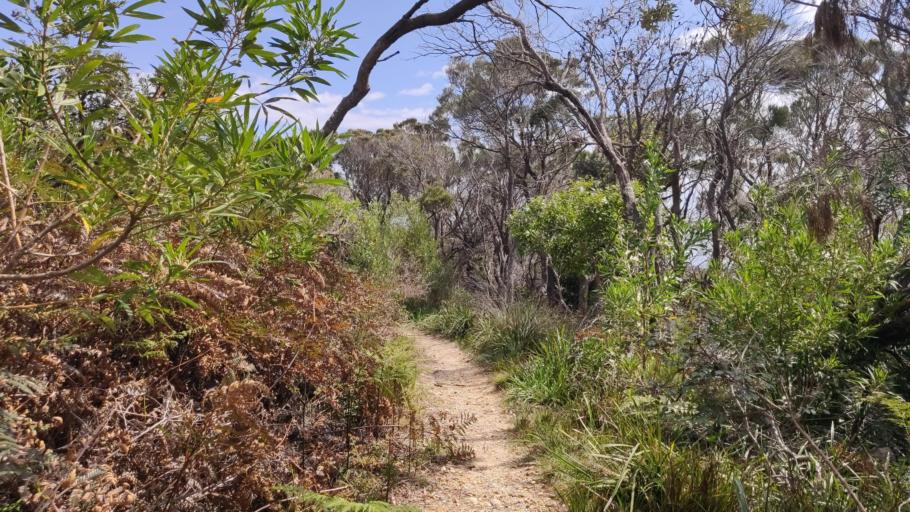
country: AU
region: New South Wales
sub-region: Port Macquarie-Hastings
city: North Haven
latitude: -31.6461
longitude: 152.8410
